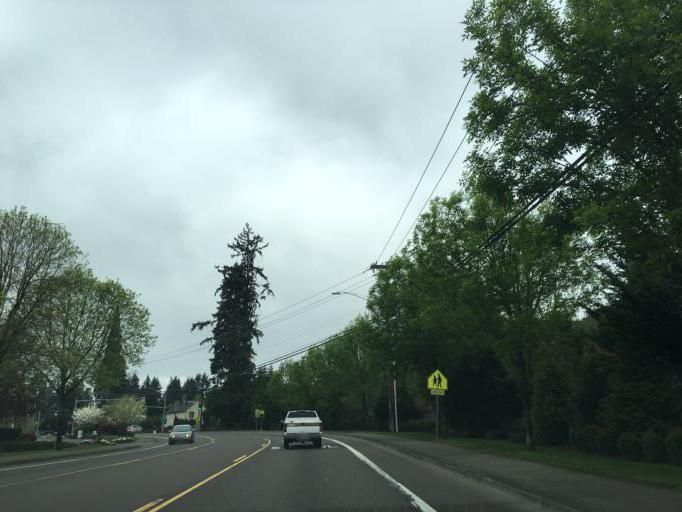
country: US
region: Oregon
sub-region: Washington County
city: Durham
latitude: 45.4039
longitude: -122.7563
